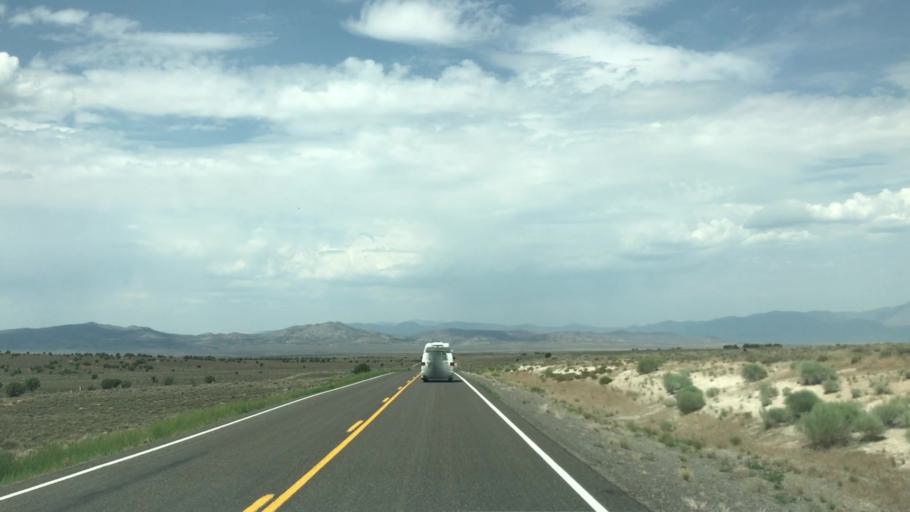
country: US
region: Nevada
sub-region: Eureka County
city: Eureka
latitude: 39.3949
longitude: -115.5305
